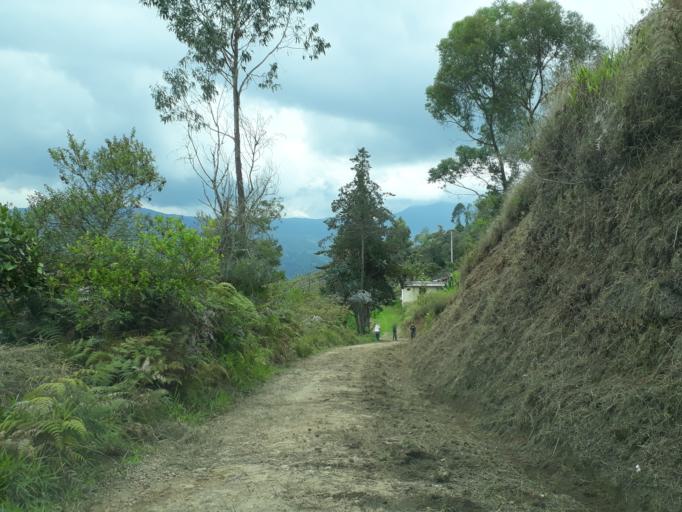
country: CO
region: Cundinamarca
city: Manta
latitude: 5.0176
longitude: -73.5431
